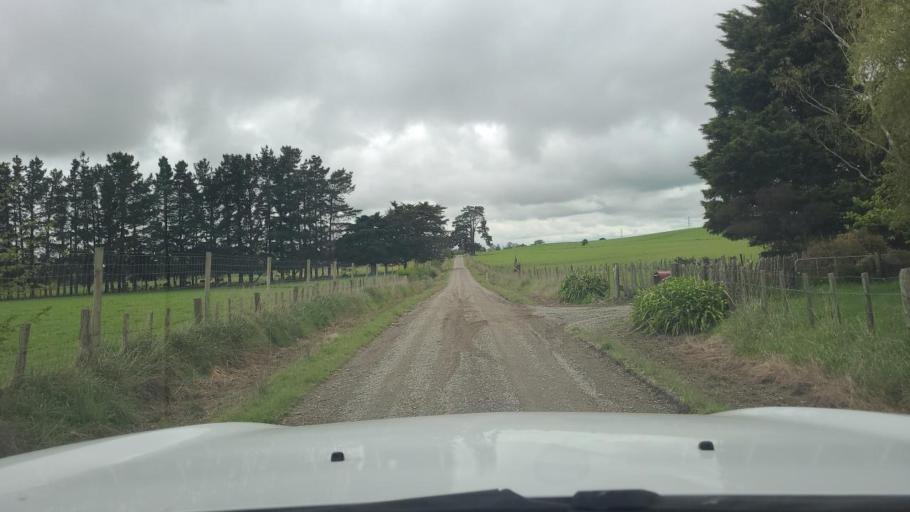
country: NZ
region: Wellington
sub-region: Masterton District
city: Masterton
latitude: -41.0515
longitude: 175.5220
